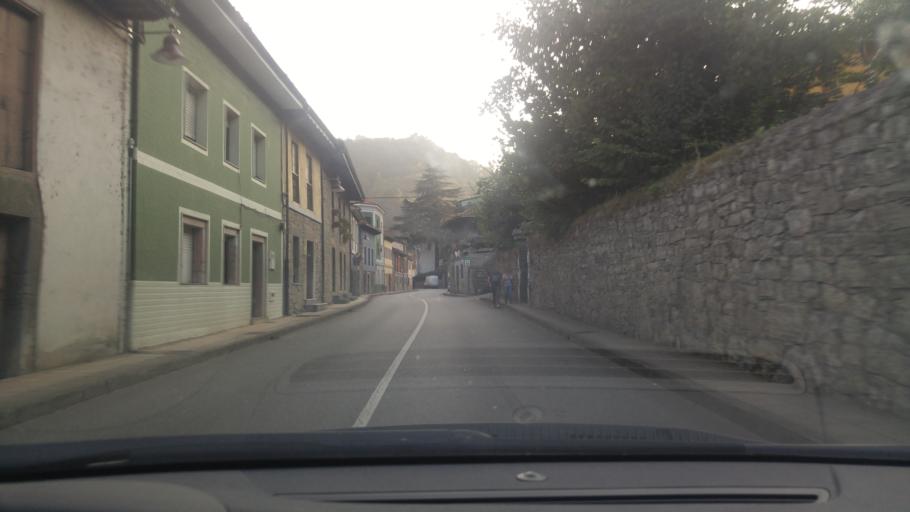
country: ES
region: Asturias
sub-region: Province of Asturias
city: Proaza
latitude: 43.2525
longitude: -6.0155
